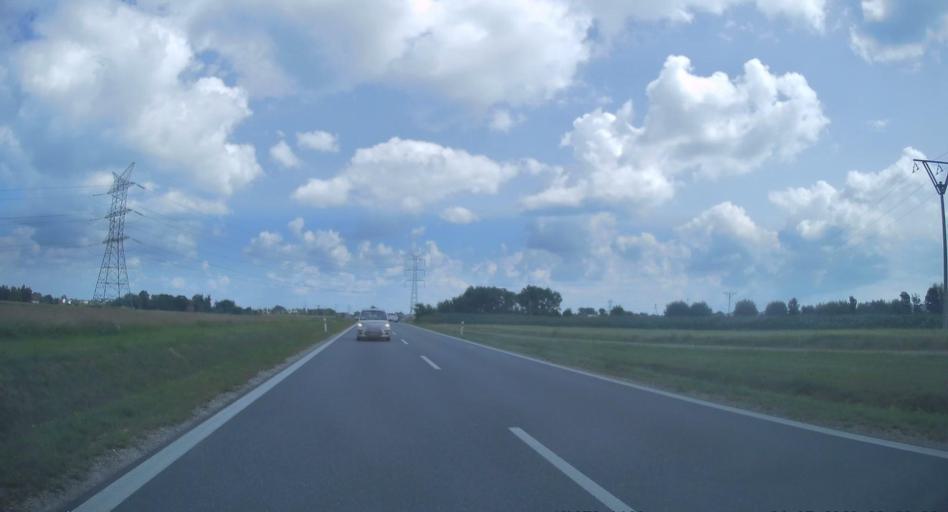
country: PL
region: Lesser Poland Voivodeship
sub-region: Powiat tarnowski
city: Wojnicz
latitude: 49.9438
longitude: 20.8462
